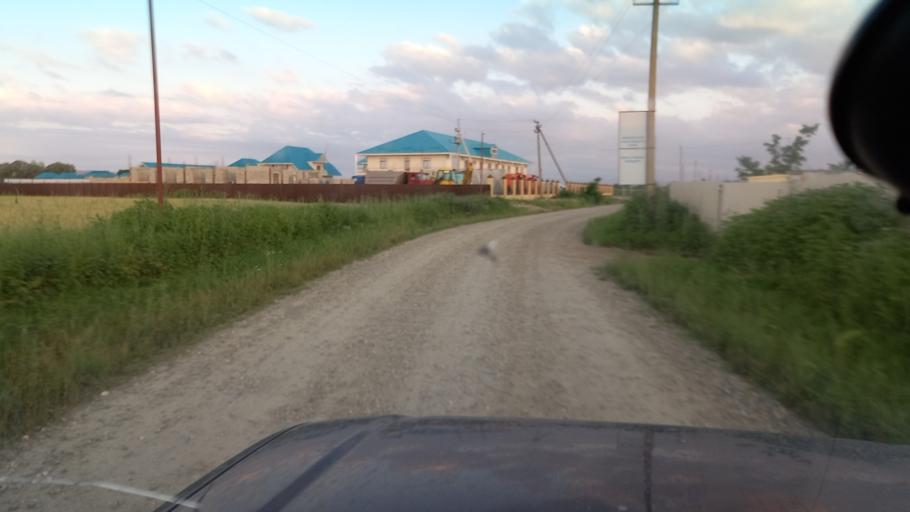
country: RU
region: Krasnodarskiy
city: Mostovskoy
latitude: 44.4380
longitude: 40.7420
